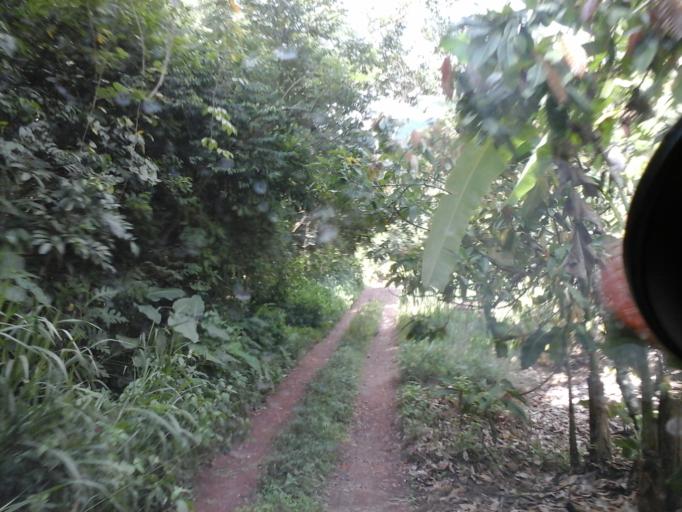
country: CO
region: Cesar
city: San Diego
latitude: 10.2879
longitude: -73.0851
